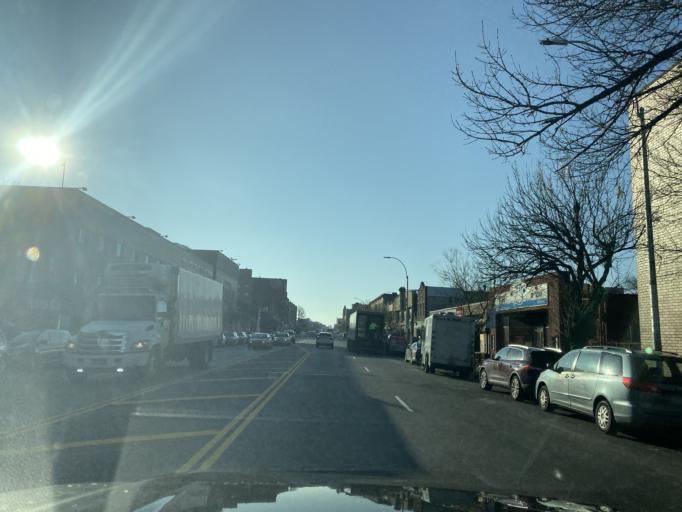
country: US
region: New York
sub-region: Kings County
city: Brooklyn
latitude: 40.6192
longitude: -73.9642
